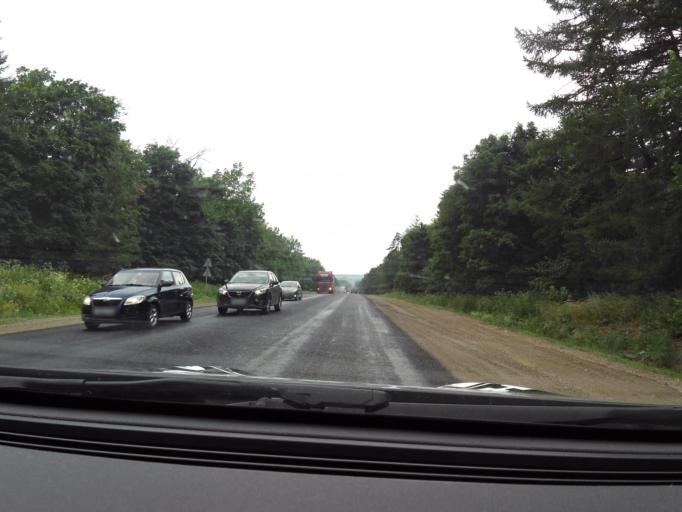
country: RU
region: Bashkortostan
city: Iglino
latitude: 54.7701
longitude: 56.4500
